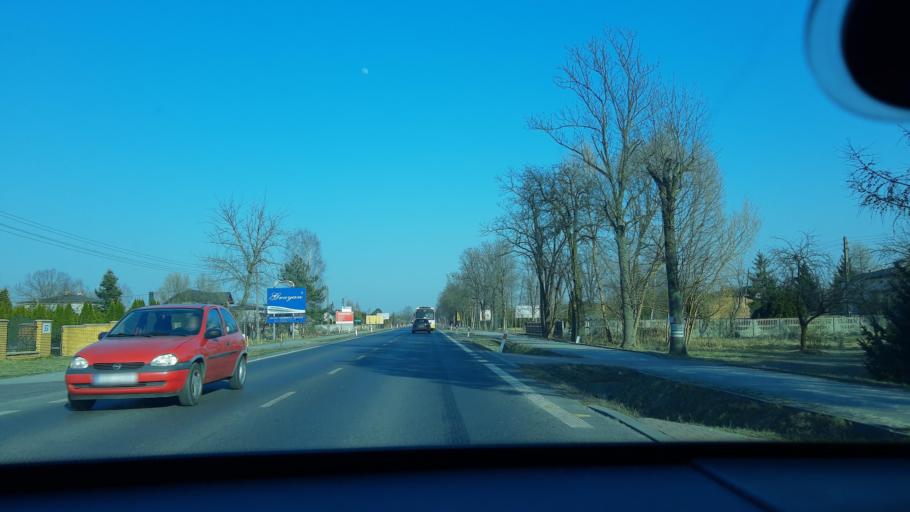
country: PL
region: Lodz Voivodeship
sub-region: Powiat zdunskowolski
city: Zapolice
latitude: 51.6043
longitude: 18.8358
